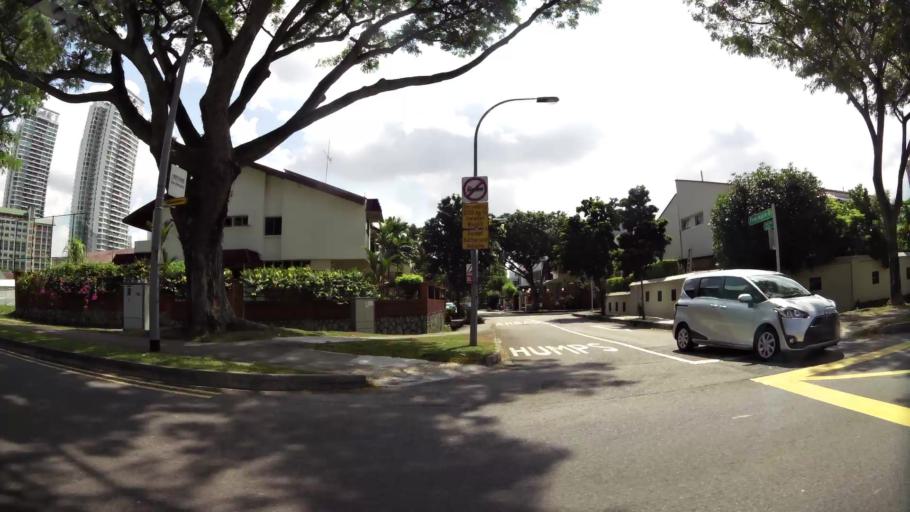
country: SG
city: Singapore
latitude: 1.3548
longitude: 103.8413
